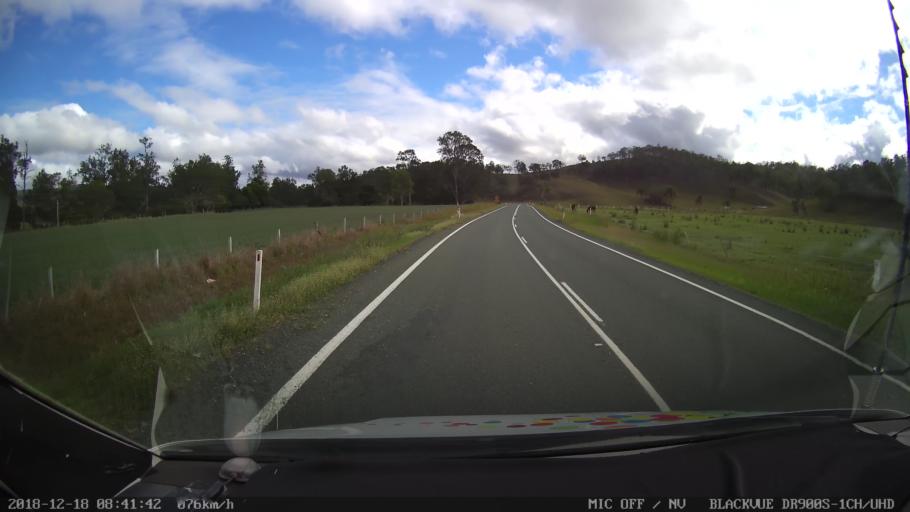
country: AU
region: Queensland
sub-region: Logan
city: Cedar Vale
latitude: -28.2338
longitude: 152.8589
